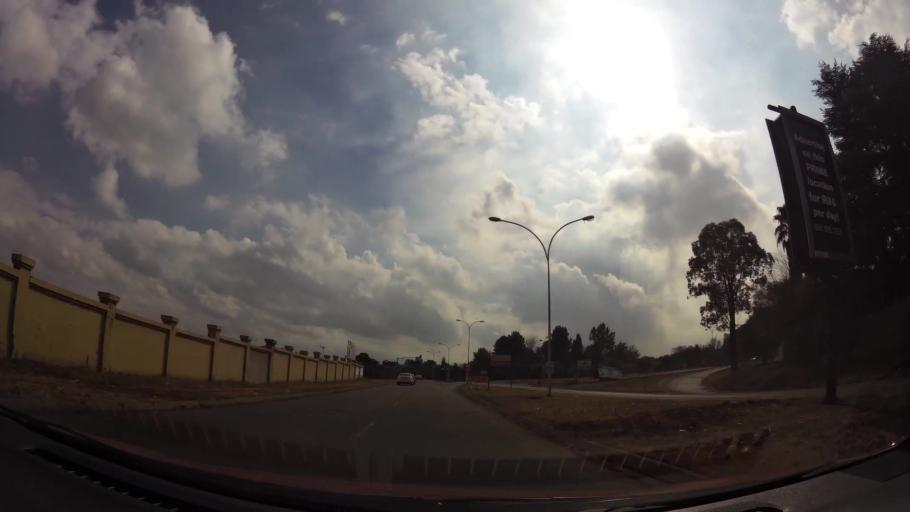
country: ZA
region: Gauteng
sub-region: Sedibeng District Municipality
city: Vanderbijlpark
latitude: -26.7355
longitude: 27.8426
